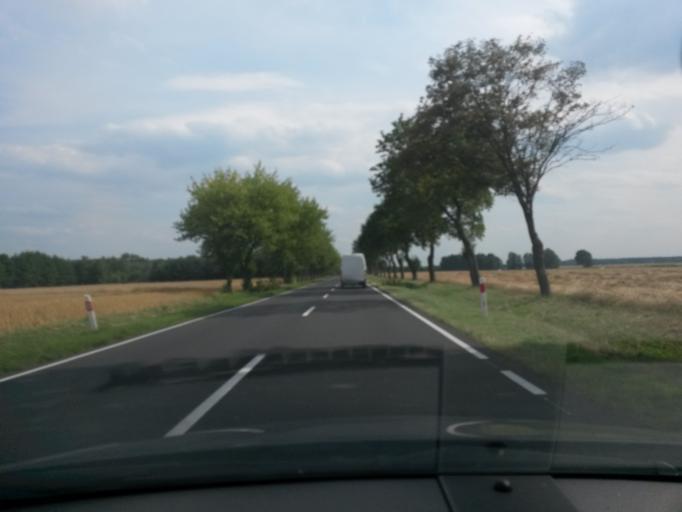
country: PL
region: Greater Poland Voivodeship
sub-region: Powiat sremski
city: Srem
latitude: 52.1423
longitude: 17.0385
